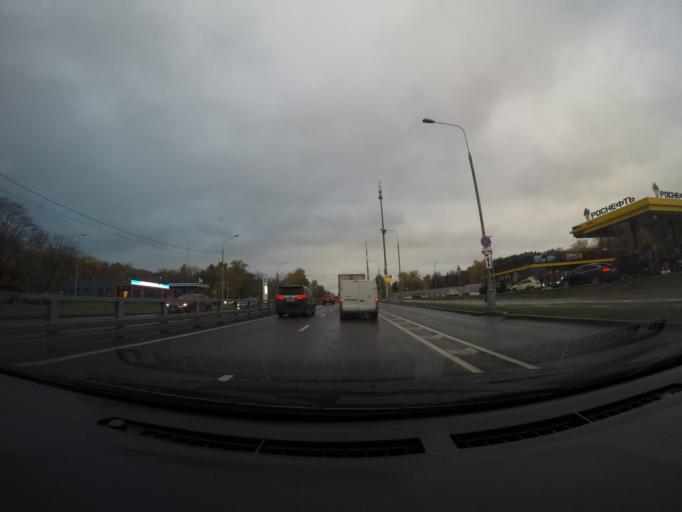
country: RU
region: Moskovskaya
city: Kastanayevo
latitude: 55.7261
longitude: 37.4957
